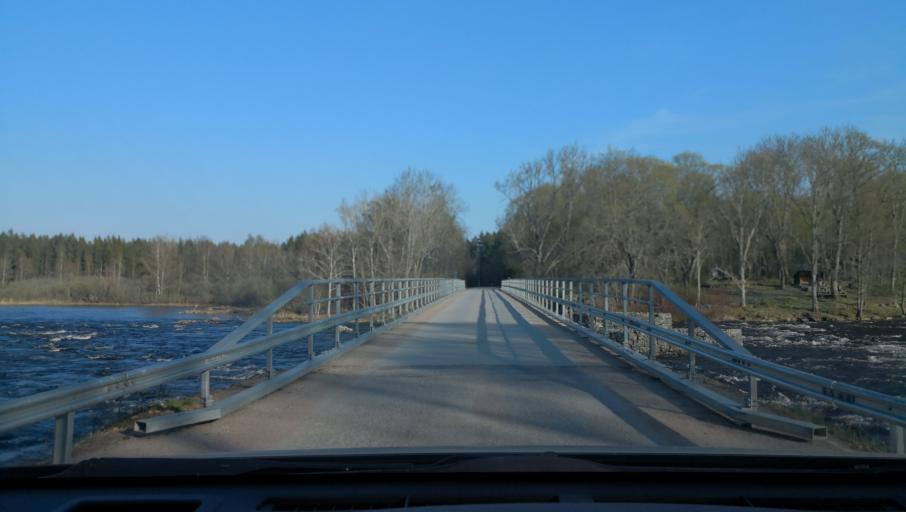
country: SE
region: Uppsala
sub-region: Heby Kommun
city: Tarnsjo
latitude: 60.2678
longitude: 16.9138
